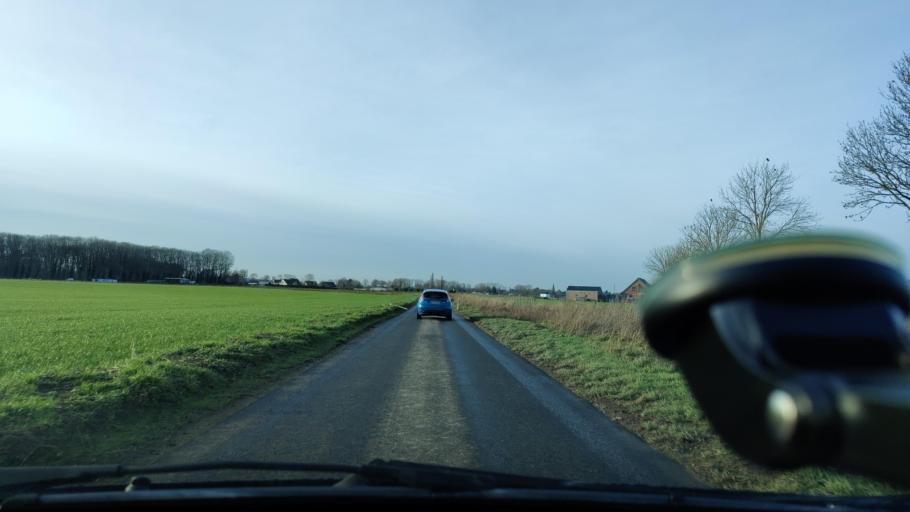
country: DE
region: North Rhine-Westphalia
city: Rees
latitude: 51.7175
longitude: 6.3662
